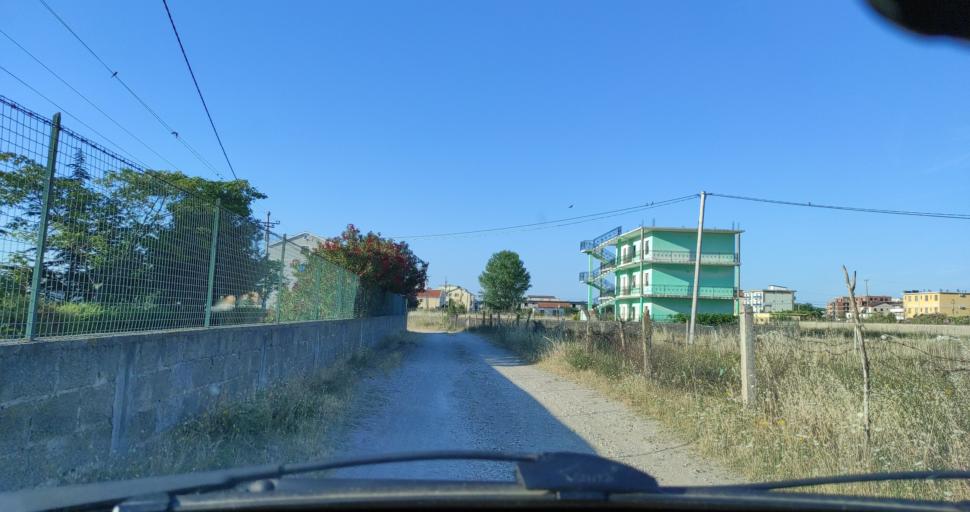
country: AL
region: Shkoder
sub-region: Rrethi i Shkodres
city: Velipoje
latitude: 41.8672
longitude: 19.4354
